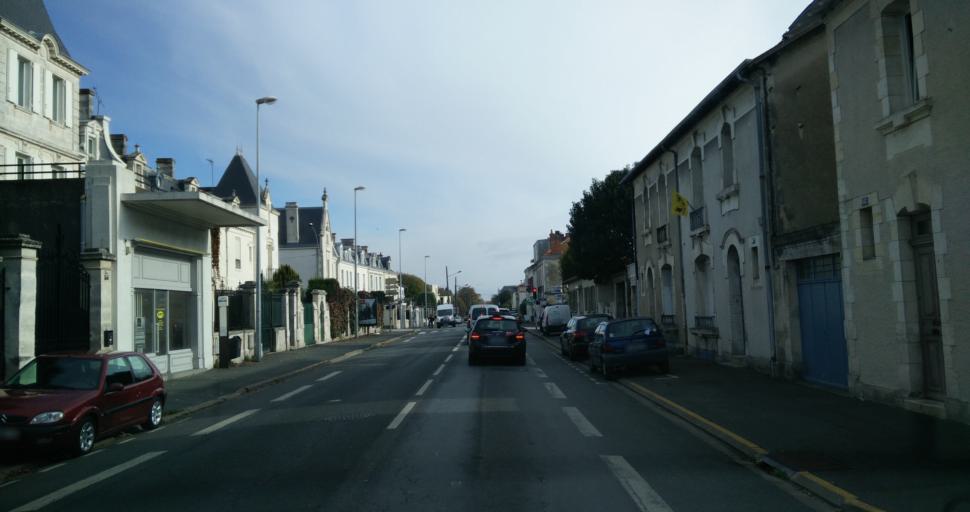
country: FR
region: Poitou-Charentes
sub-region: Departement de la Charente-Maritime
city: La Rochelle
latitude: 46.1632
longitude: -1.1661
